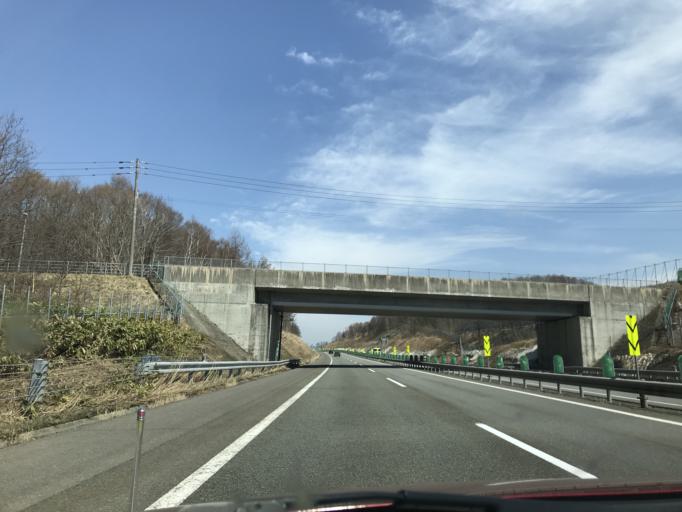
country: JP
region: Hokkaido
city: Iwamizawa
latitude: 43.2026
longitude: 141.8123
